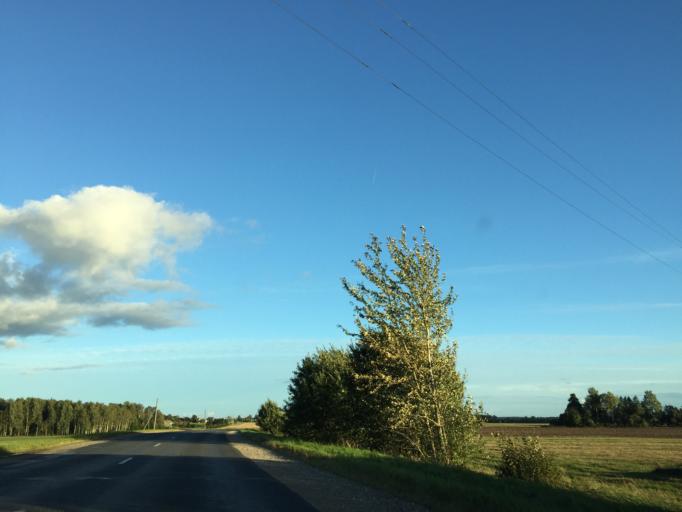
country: LV
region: Saldus Rajons
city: Saldus
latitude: 56.7050
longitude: 22.4262
